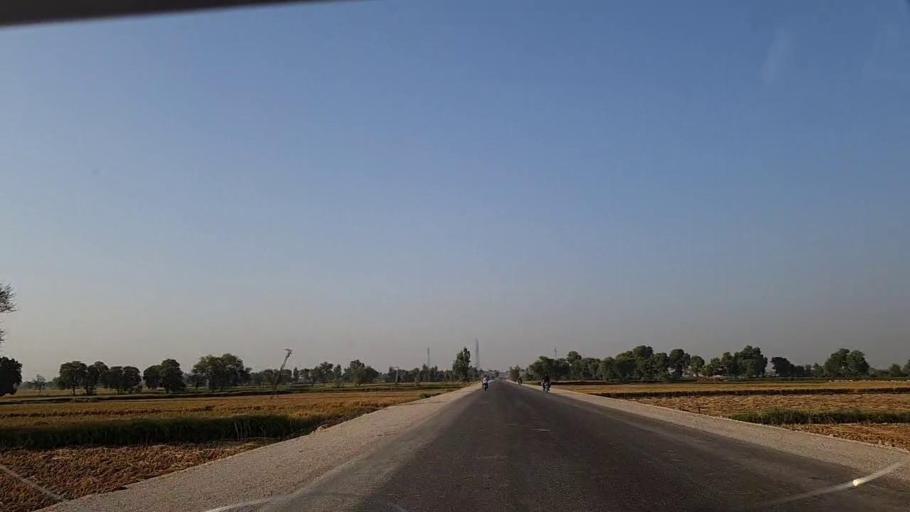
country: PK
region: Sindh
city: Rustam jo Goth
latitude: 27.9563
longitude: 68.8077
